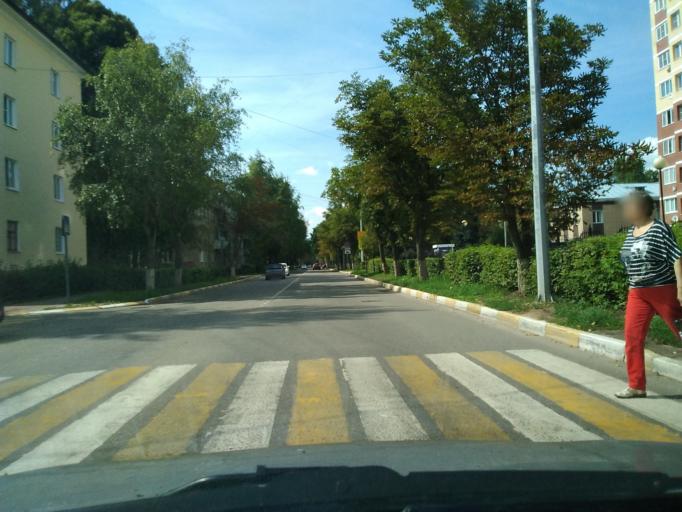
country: RU
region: Moskovskaya
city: Voskresensk
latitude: 55.3254
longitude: 38.6663
